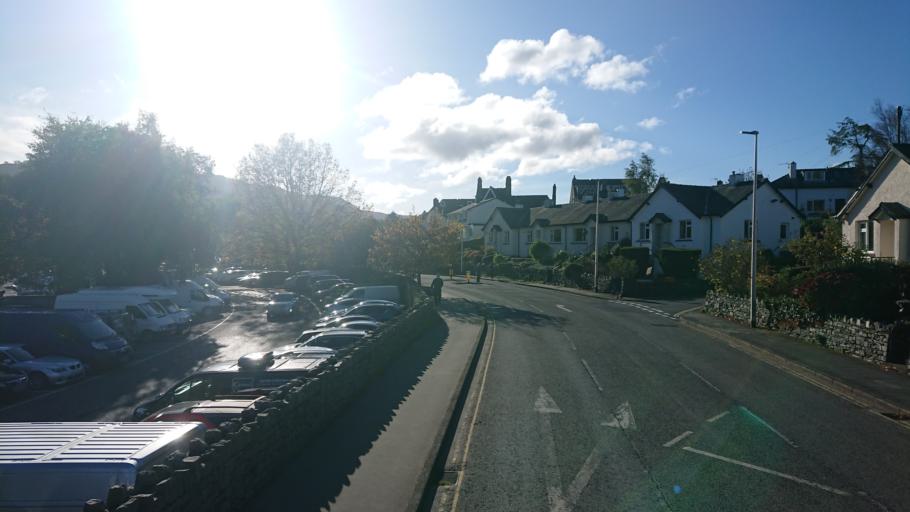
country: GB
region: England
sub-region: Cumbria
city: Keswick
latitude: 54.6005
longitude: -3.1393
